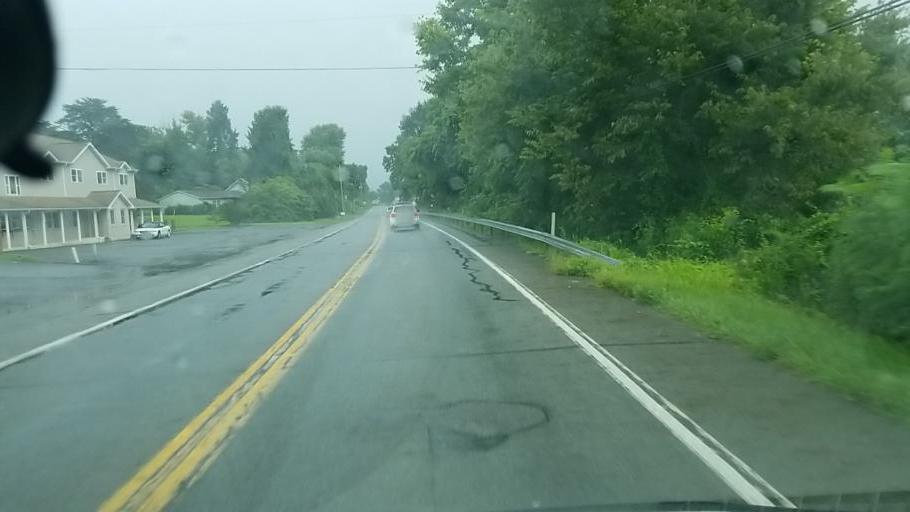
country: US
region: Pennsylvania
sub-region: Dauphin County
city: Millersburg
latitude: 40.5093
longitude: -76.9631
